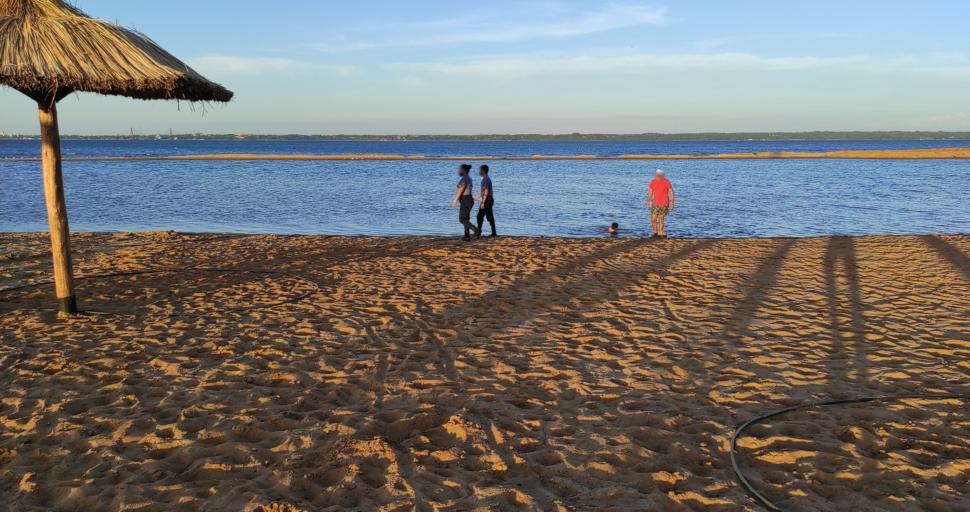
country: AR
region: Misiones
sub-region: Departamento de Capital
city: Posadas
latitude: -27.4190
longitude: -55.8788
